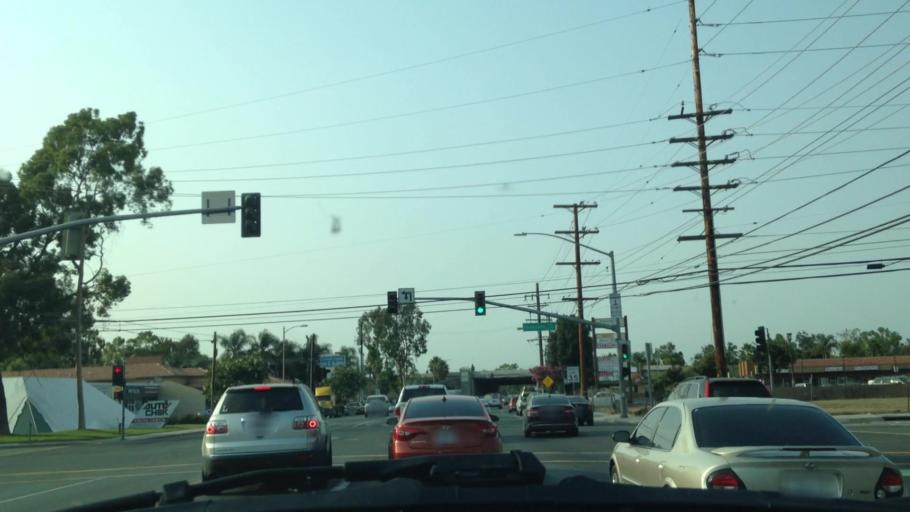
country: US
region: California
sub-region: Orange County
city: Orange
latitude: 33.7730
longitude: -117.8528
